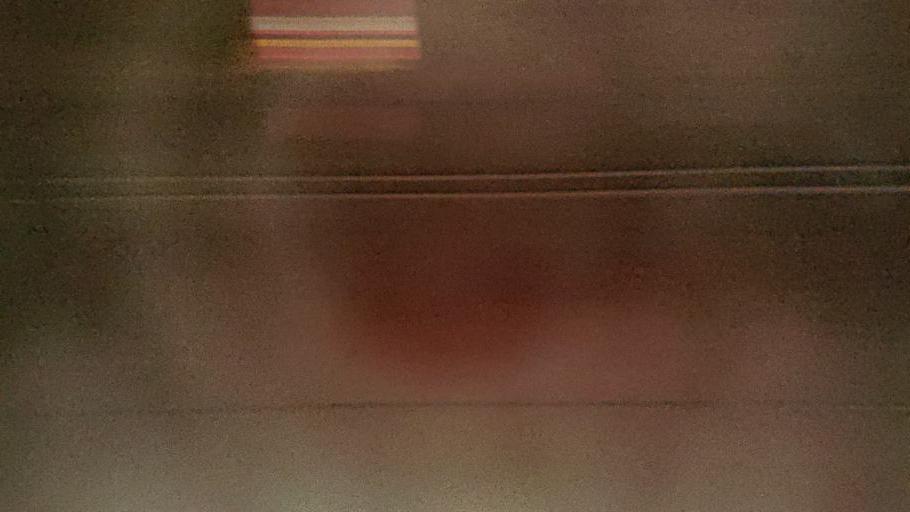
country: TW
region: Taiwan
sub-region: Keelung
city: Keelung
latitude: 25.0883
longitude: 121.7065
